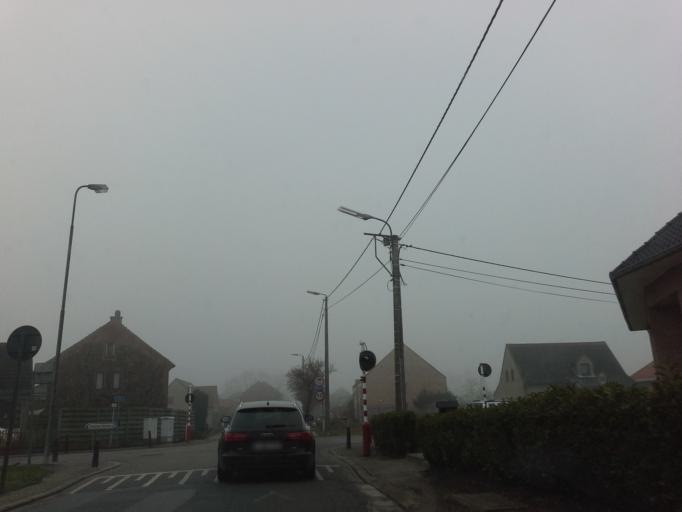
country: BE
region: Flanders
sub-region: Provincie Vlaams-Brabant
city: Holsbeek
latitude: 50.8761
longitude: 4.7627
